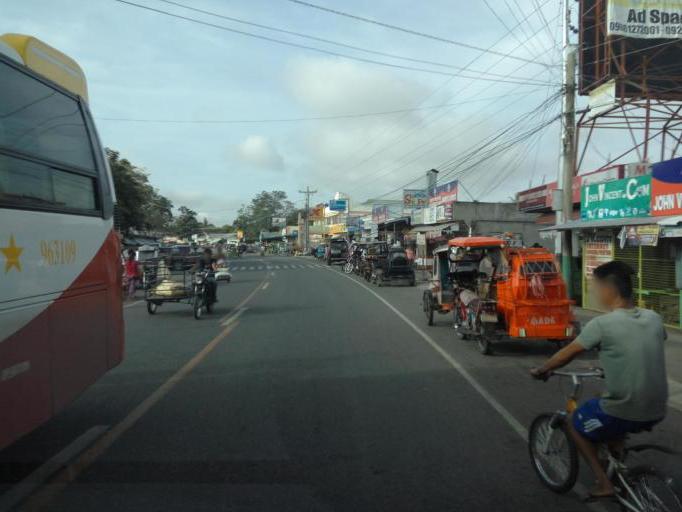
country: PH
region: Cagayan Valley
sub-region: Province of Isabela
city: Cabagan
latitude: 17.4285
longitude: 121.7728
